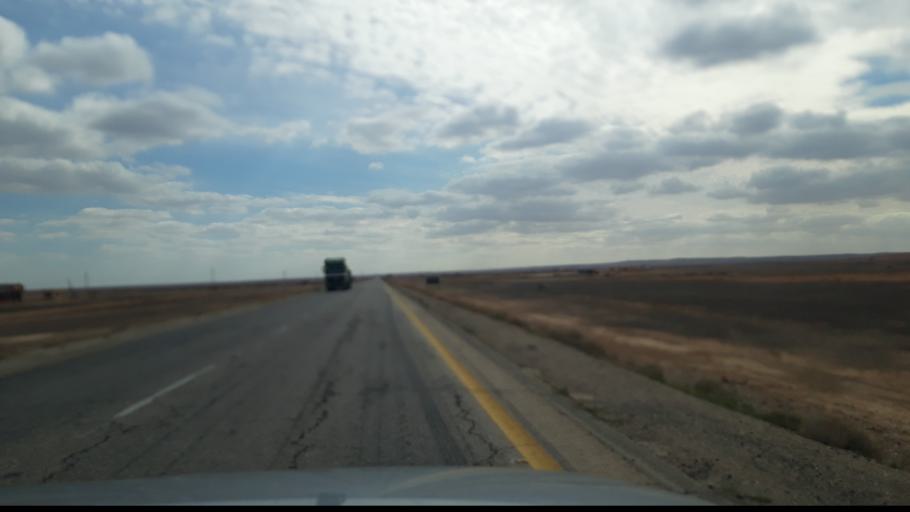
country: JO
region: Amman
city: Al Azraq ash Shamali
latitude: 31.8066
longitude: 36.5931
